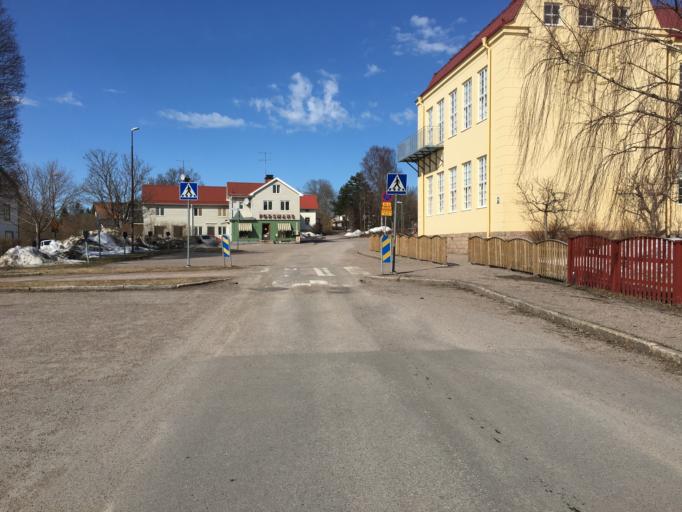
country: SE
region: Gaevleborg
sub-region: Hofors Kommun
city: Hofors
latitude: 60.5098
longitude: 16.4695
